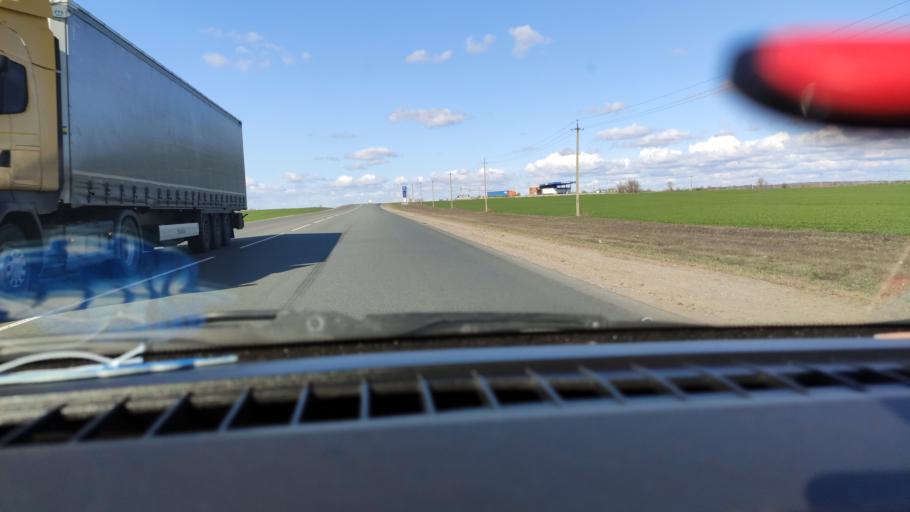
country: RU
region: Samara
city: Varlamovo
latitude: 53.2116
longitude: 48.4533
